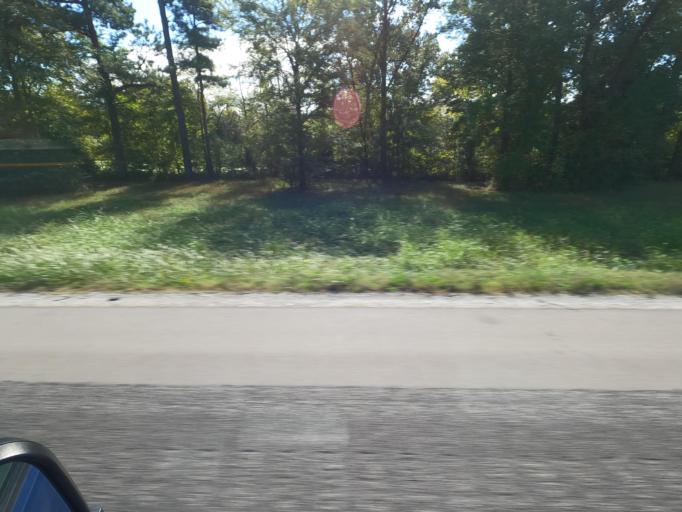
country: US
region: Tennessee
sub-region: Crockett County
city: Bells
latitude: 35.6265
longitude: -88.9703
